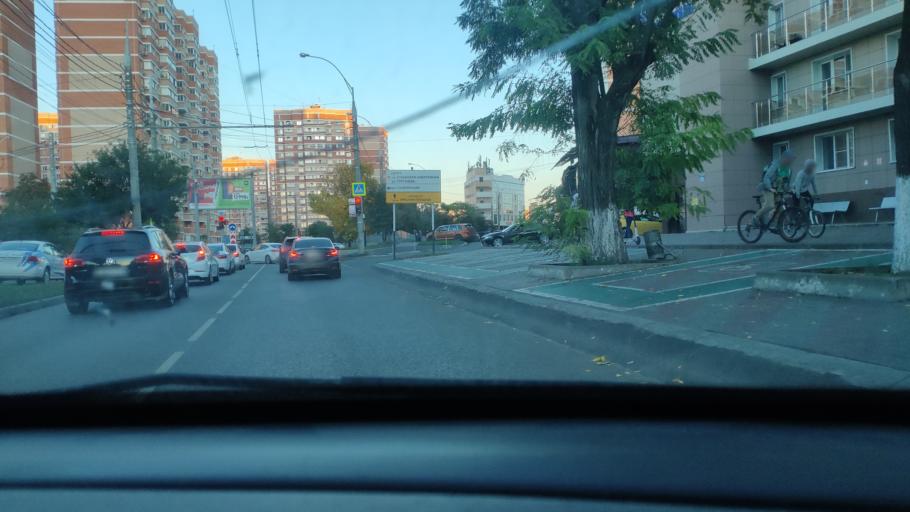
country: RU
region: Krasnodarskiy
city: Krasnodar
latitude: 45.0386
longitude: 38.9474
